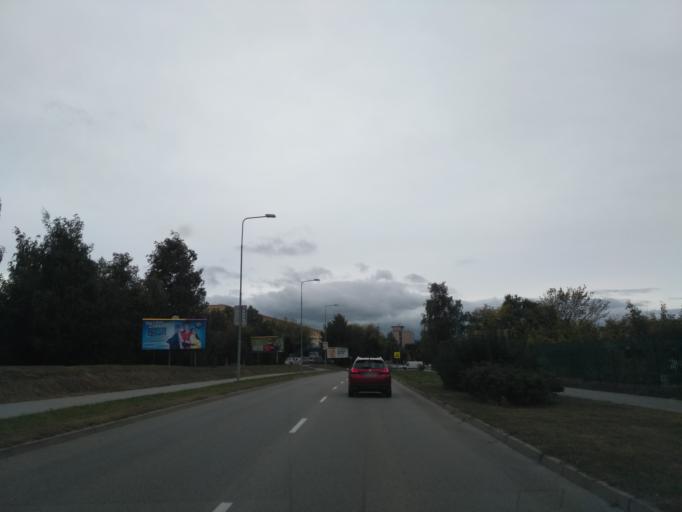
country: SK
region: Kosicky
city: Kosice
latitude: 48.7090
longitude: 21.2285
